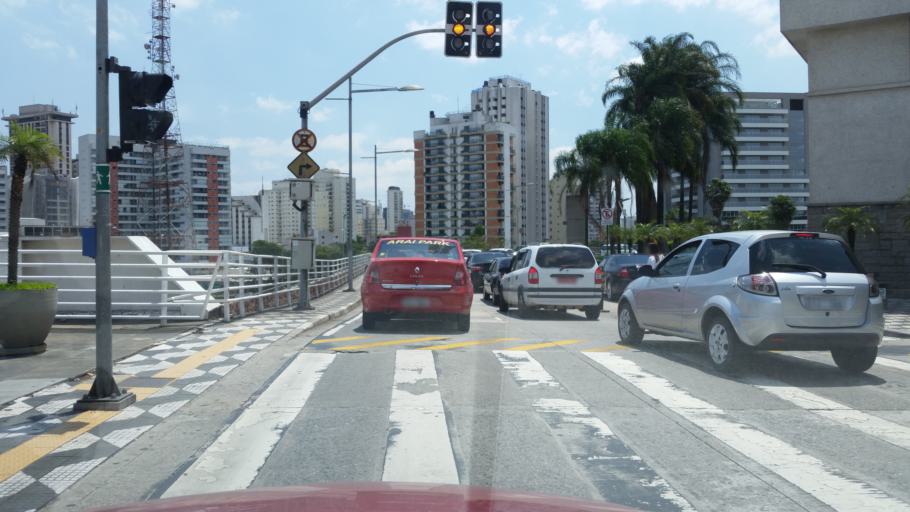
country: BR
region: Sao Paulo
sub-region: Diadema
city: Diadema
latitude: -23.6262
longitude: -46.6604
